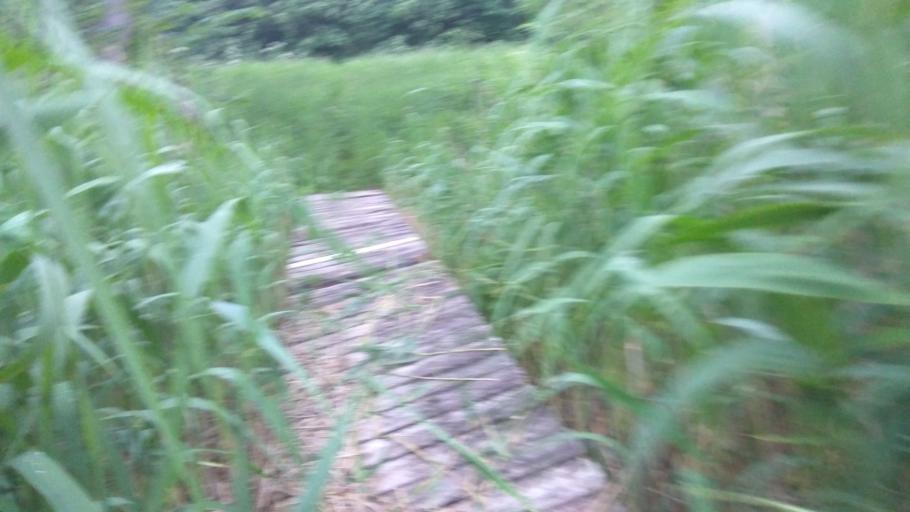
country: LV
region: Kuldigas Rajons
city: Kuldiga
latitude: 56.8751
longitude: 21.8216
